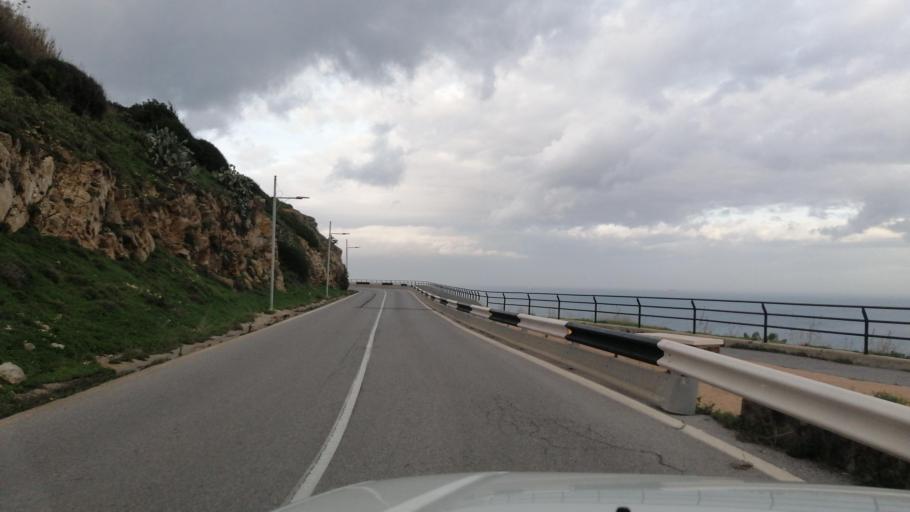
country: ES
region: Ceuta
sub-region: Ceuta
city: Ceuta
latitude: 35.8977
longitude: -5.2805
